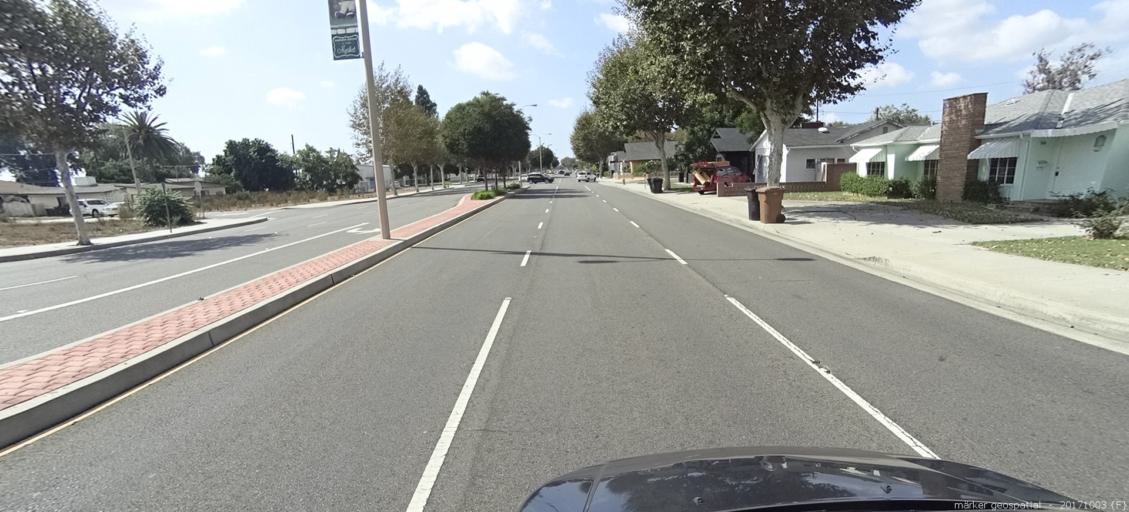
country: US
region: California
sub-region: Orange County
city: Garden Grove
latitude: 33.7743
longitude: -117.9334
